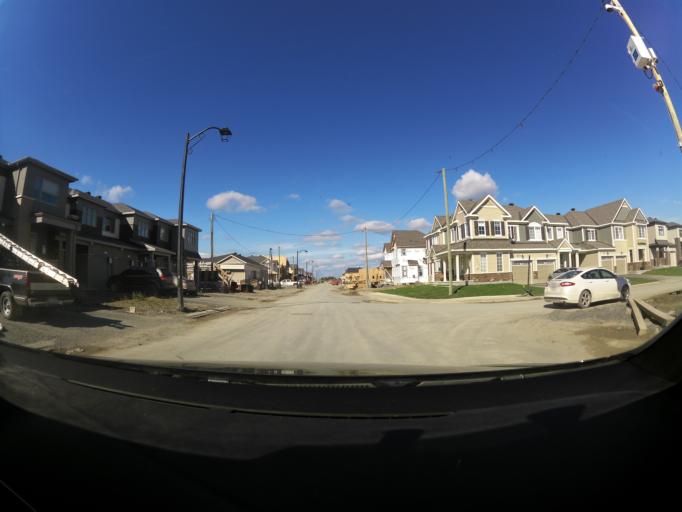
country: CA
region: Ontario
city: Bells Corners
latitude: 45.2810
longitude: -75.8904
